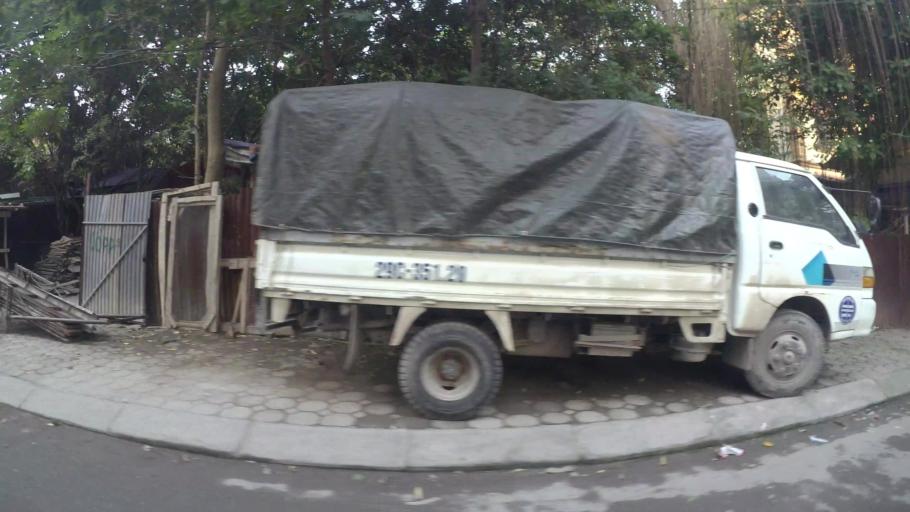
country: VN
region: Ha Noi
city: Tay Ho
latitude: 21.0680
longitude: 105.7918
